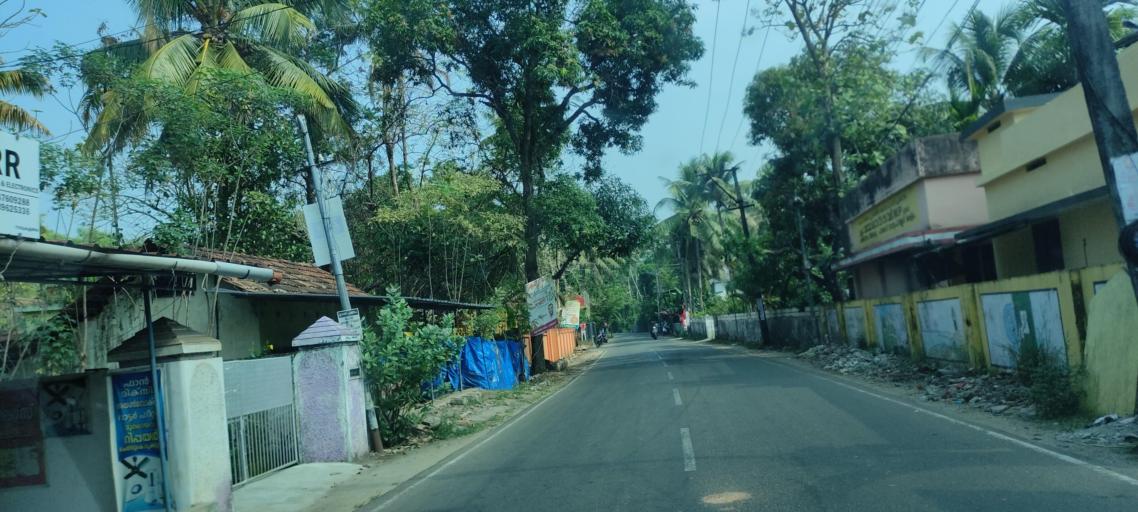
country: IN
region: Kerala
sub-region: Alappuzha
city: Kutiatodu
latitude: 9.7813
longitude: 76.3046
